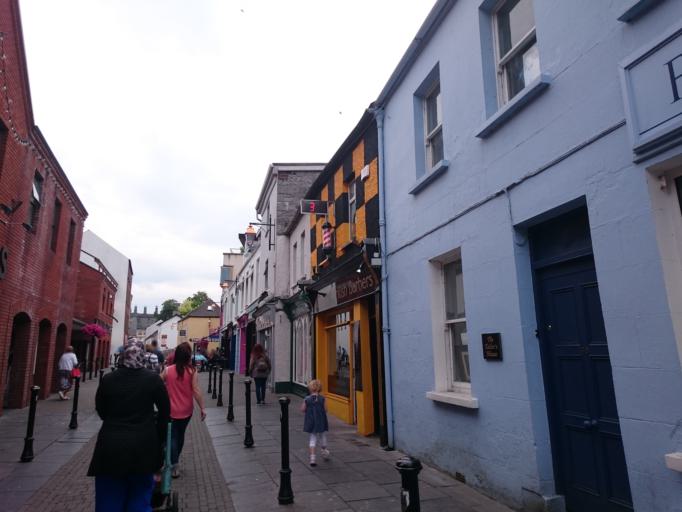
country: IE
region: Leinster
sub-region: Kilkenny
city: Kilkenny
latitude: 52.6528
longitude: -7.2529
